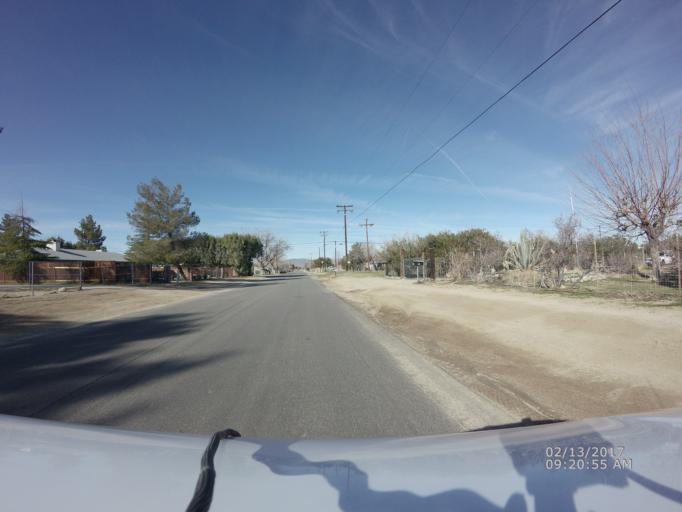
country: US
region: California
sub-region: Los Angeles County
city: Littlerock
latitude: 34.5303
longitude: -117.9663
